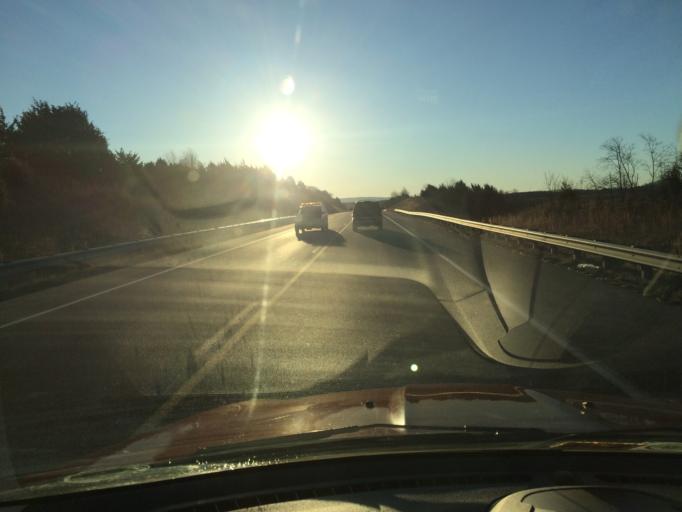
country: US
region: Virginia
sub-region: Augusta County
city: Verona
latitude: 38.1763
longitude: -79.0250
